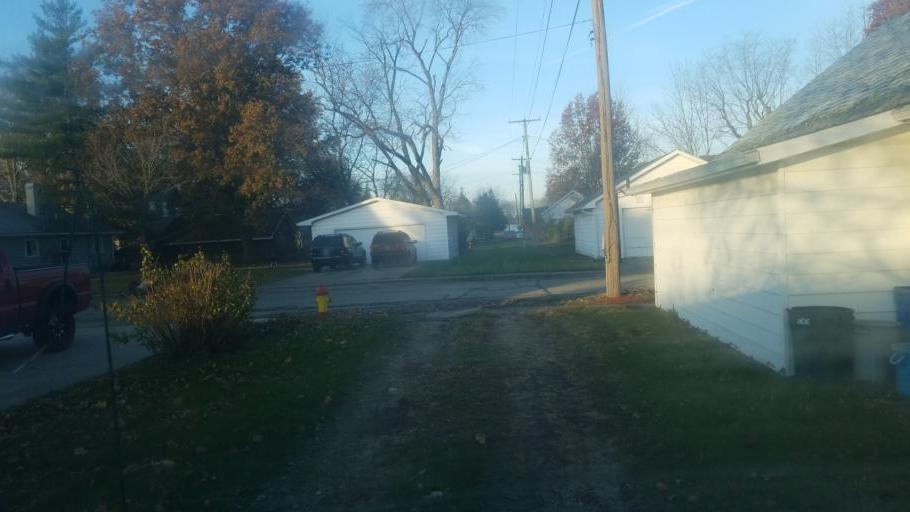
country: US
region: Indiana
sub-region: Adams County
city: Berne
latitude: 40.6572
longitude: -84.9582
